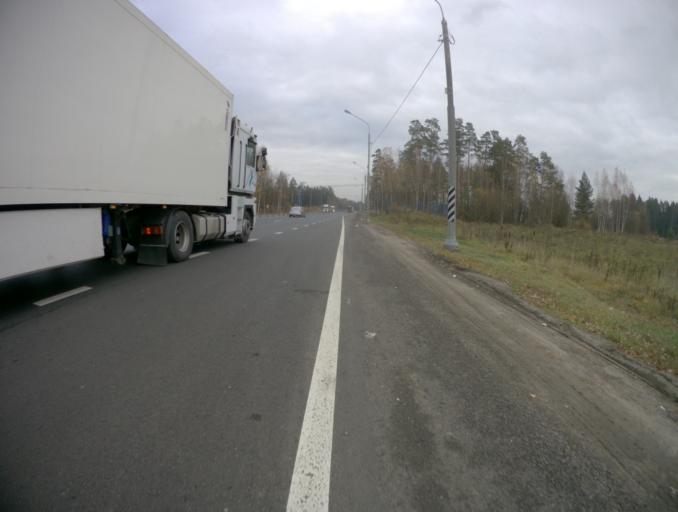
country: RU
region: Moskovskaya
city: Malaya Dubna
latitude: 55.8511
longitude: 38.9637
